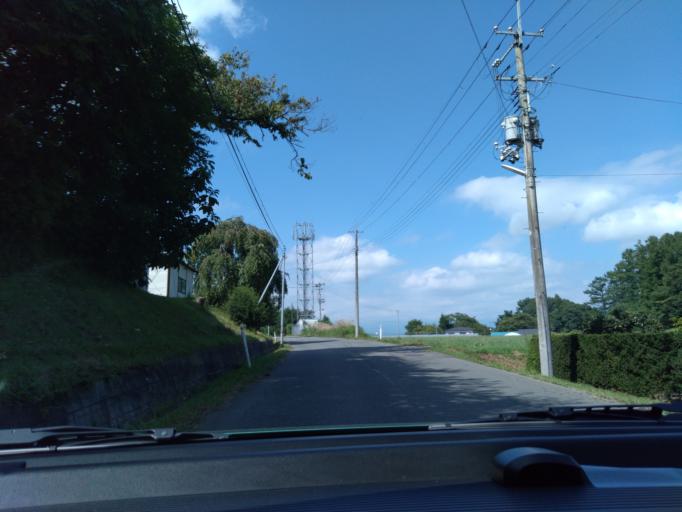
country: JP
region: Iwate
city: Shizukuishi
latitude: 39.6705
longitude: 140.9687
